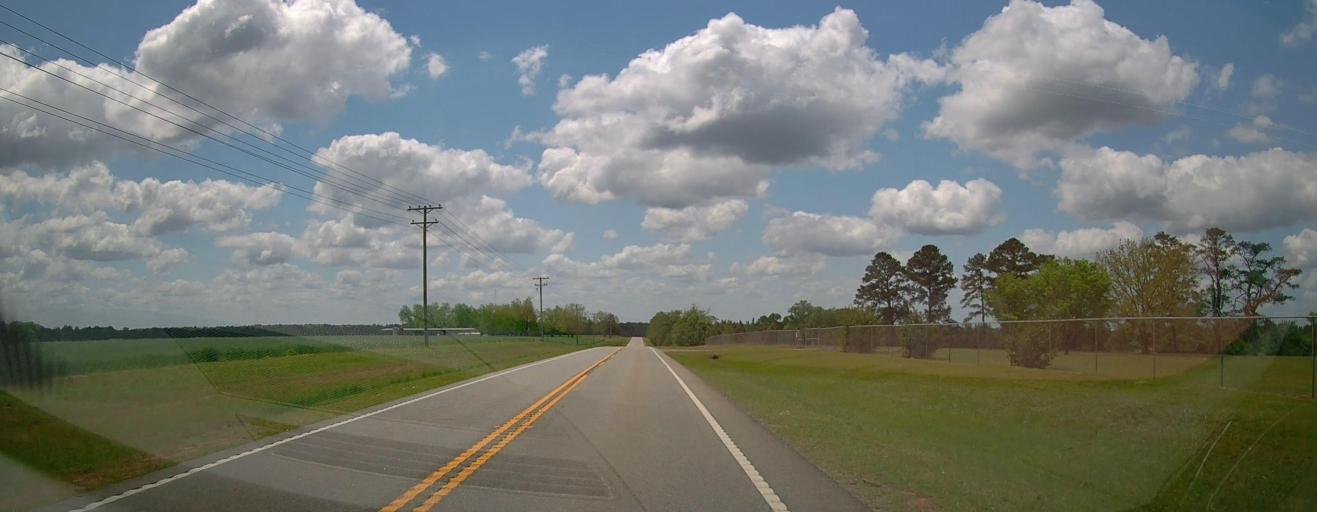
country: US
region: Georgia
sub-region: Laurens County
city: Dublin
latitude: 32.5614
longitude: -83.0416
